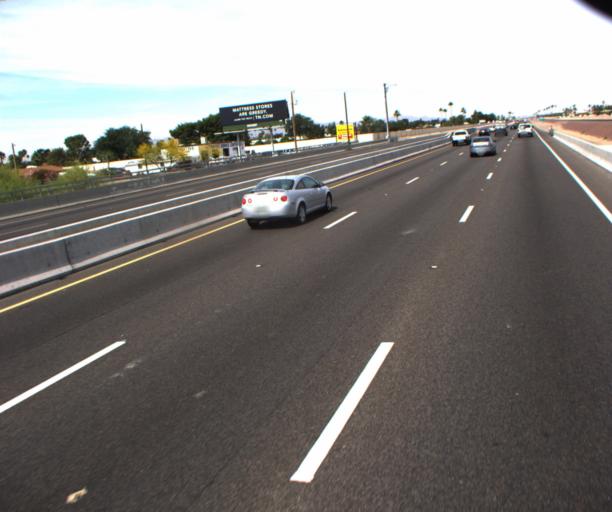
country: US
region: Arizona
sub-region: Maricopa County
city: Sun City
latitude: 33.5948
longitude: -112.2623
